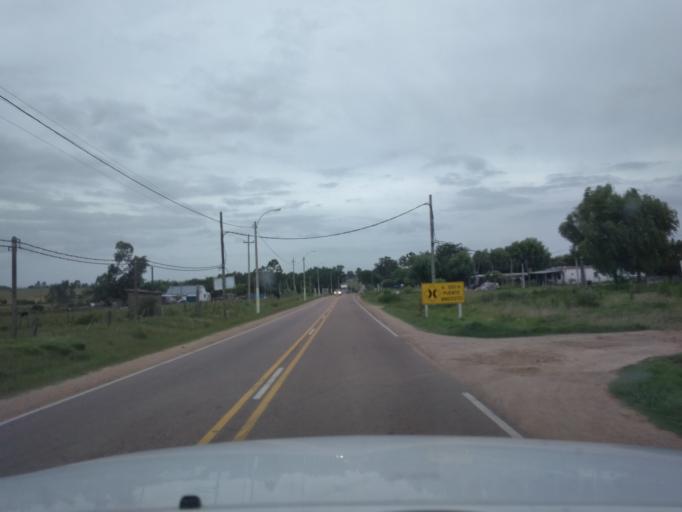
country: UY
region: Canelones
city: Tala
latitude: -34.3511
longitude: -55.7681
